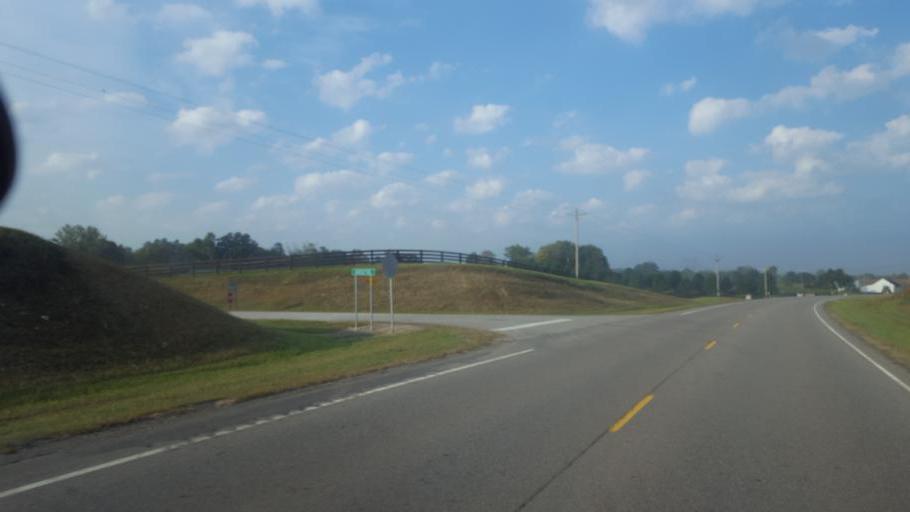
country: US
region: Ohio
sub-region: Licking County
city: Utica
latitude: 40.2271
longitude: -82.5063
